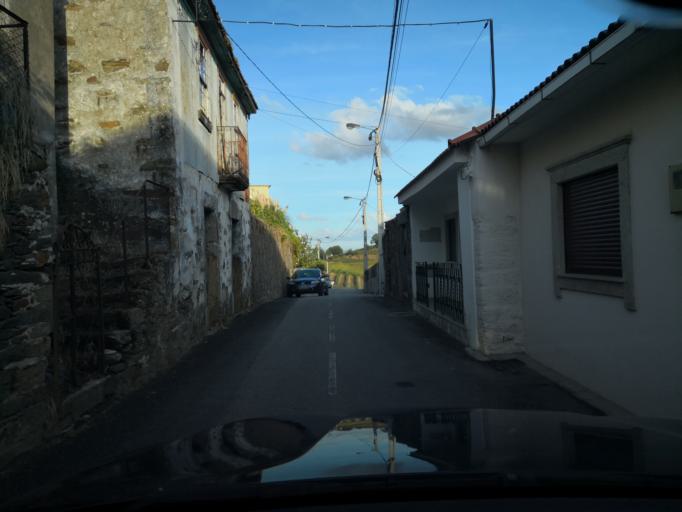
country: PT
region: Vila Real
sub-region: Santa Marta de Penaguiao
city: Santa Marta de Penaguiao
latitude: 41.2289
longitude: -7.8096
